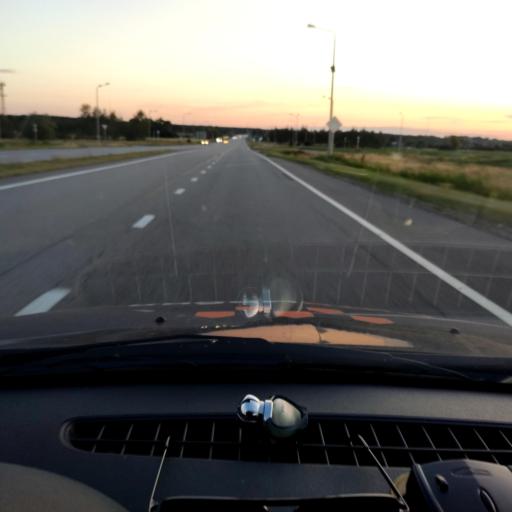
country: RU
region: Belgorod
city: Gubkin
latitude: 51.1865
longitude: 37.4048
